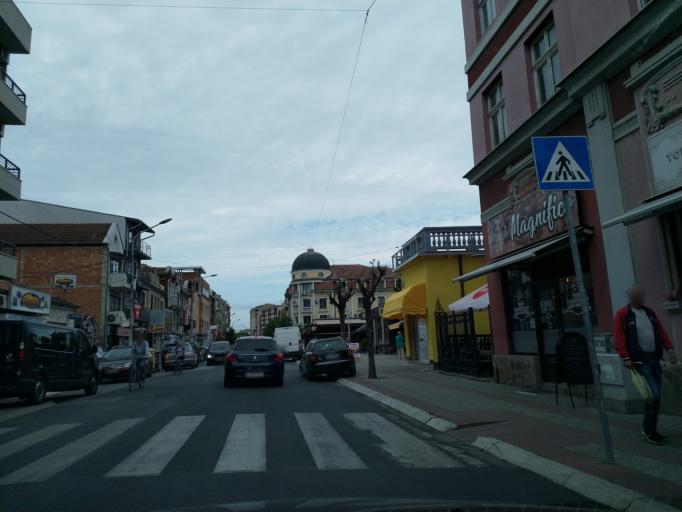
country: RS
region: Central Serbia
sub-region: Pomoravski Okrug
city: Jagodina
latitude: 43.9771
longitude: 21.2624
